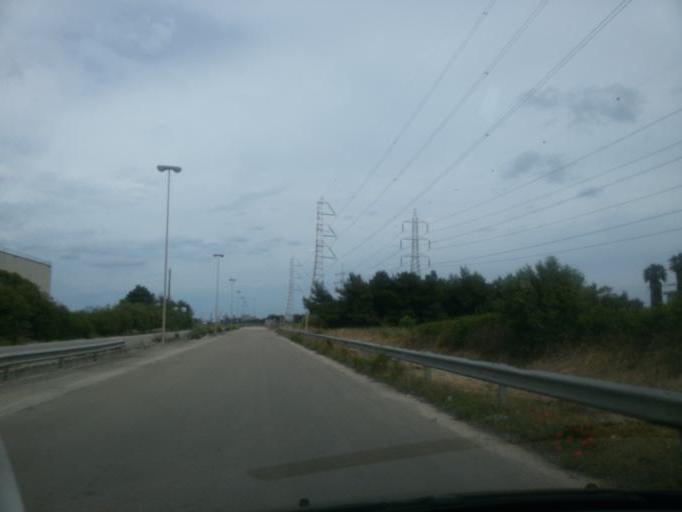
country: IT
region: Apulia
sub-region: Provincia di Brindisi
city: Materdomini
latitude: 40.6342
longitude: 17.9779
